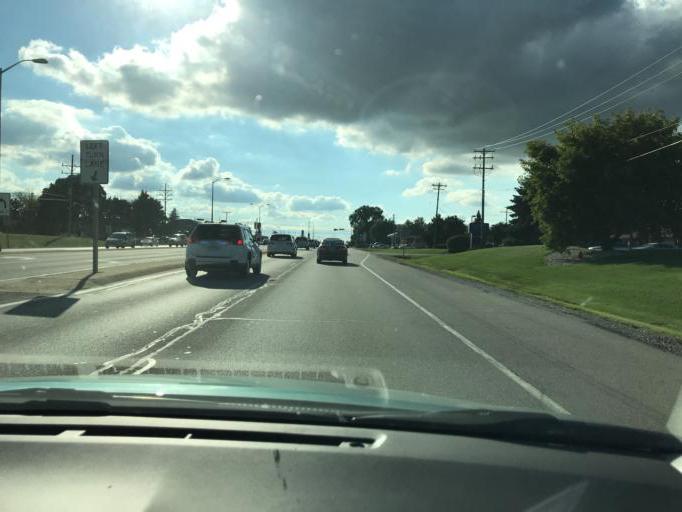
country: US
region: Wisconsin
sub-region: Kenosha County
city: Pleasant Prairie
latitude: 42.5669
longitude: -87.9118
